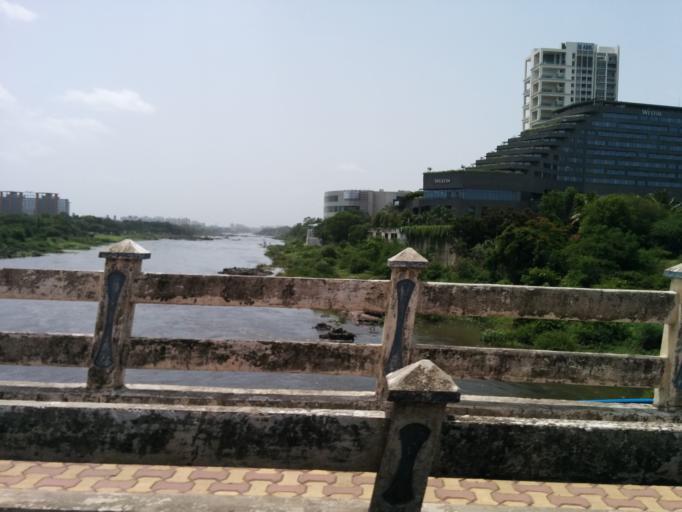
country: IN
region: Maharashtra
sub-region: Pune Division
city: Shivaji Nagar
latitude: 18.5411
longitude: 73.9042
